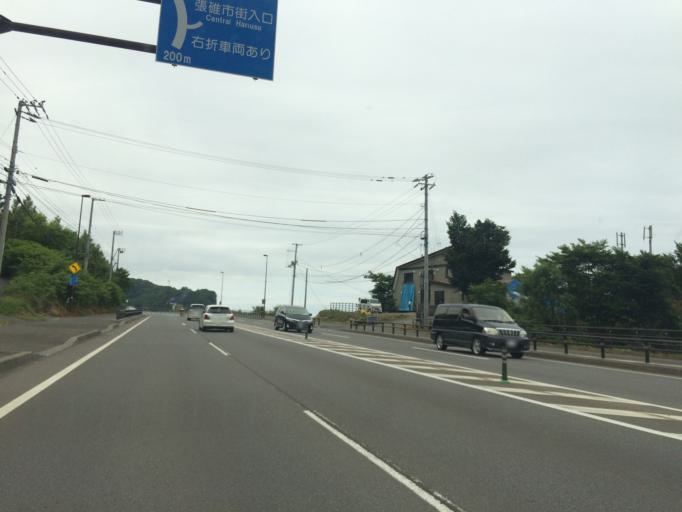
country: JP
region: Hokkaido
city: Otaru
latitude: 43.1523
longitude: 141.1297
